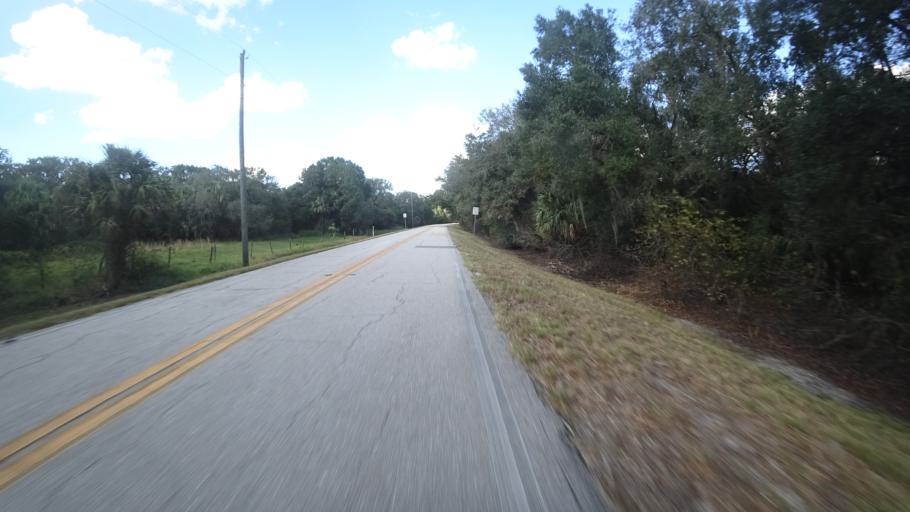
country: US
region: Florida
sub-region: Sarasota County
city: North Port
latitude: 27.2139
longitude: -82.1221
